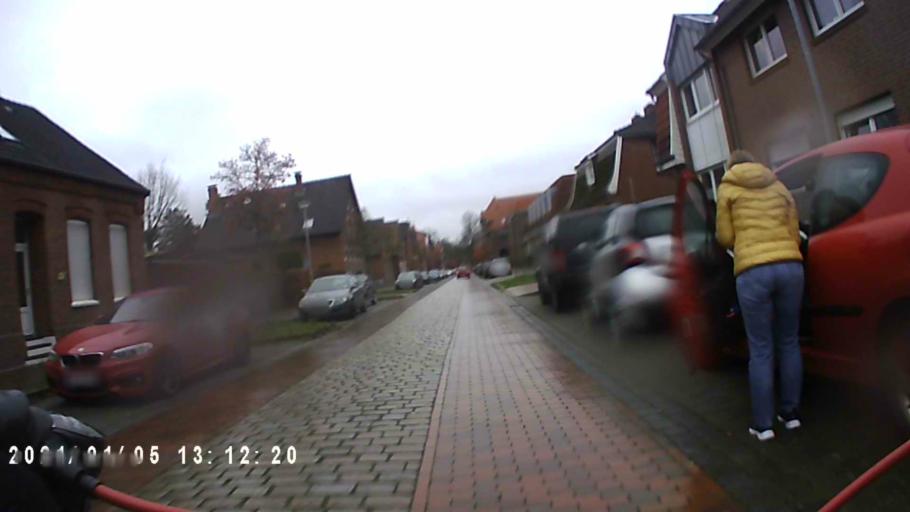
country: DE
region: Lower Saxony
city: Leer
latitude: 53.2352
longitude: 7.4622
